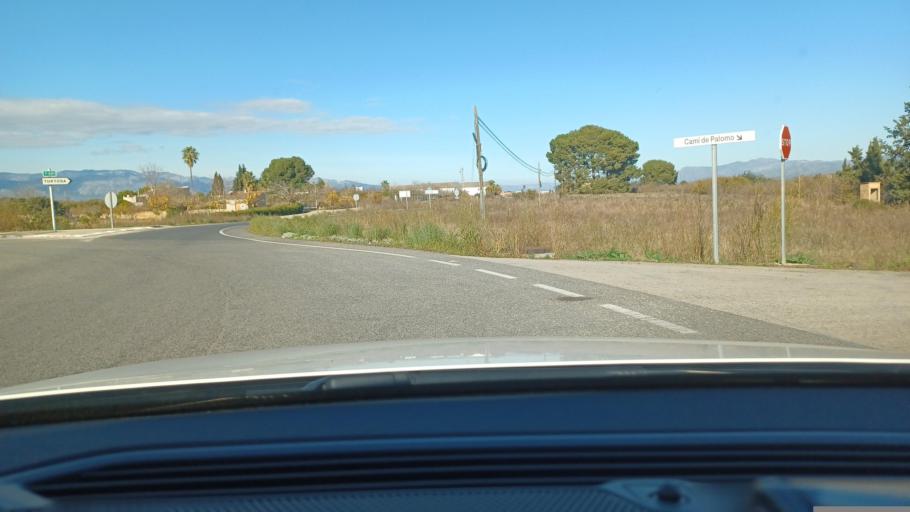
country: ES
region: Catalonia
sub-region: Provincia de Tarragona
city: Santa Barbara
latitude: 40.7232
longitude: 0.5033
